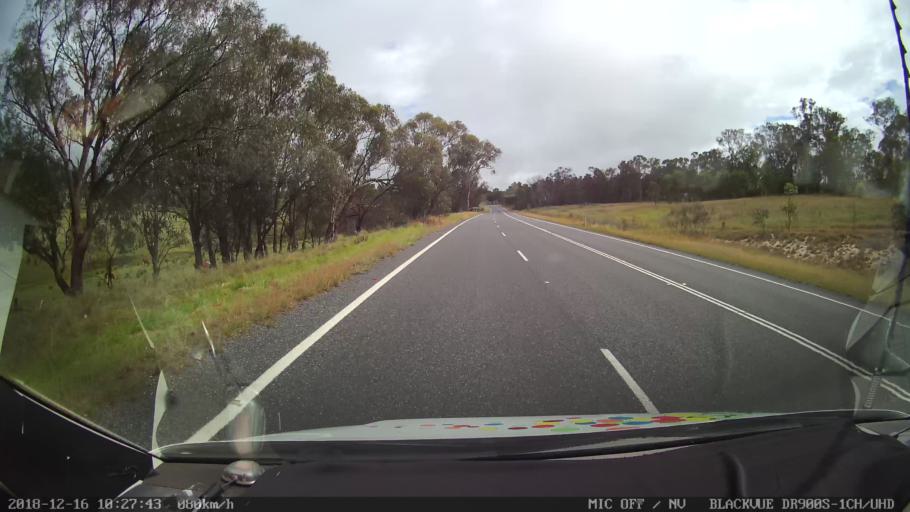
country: AU
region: New South Wales
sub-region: Tenterfield Municipality
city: Carrolls Creek
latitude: -29.1301
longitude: 151.9959
